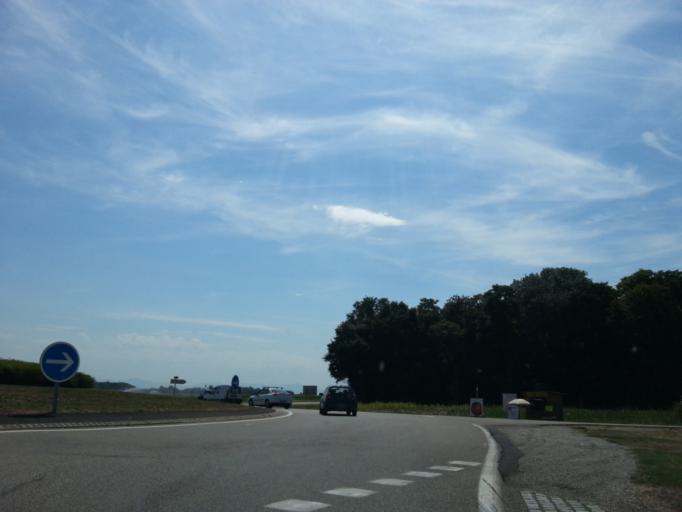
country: FR
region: Alsace
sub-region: Departement du Haut-Rhin
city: Horbourg-Wihr
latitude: 48.0661
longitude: 7.3938
